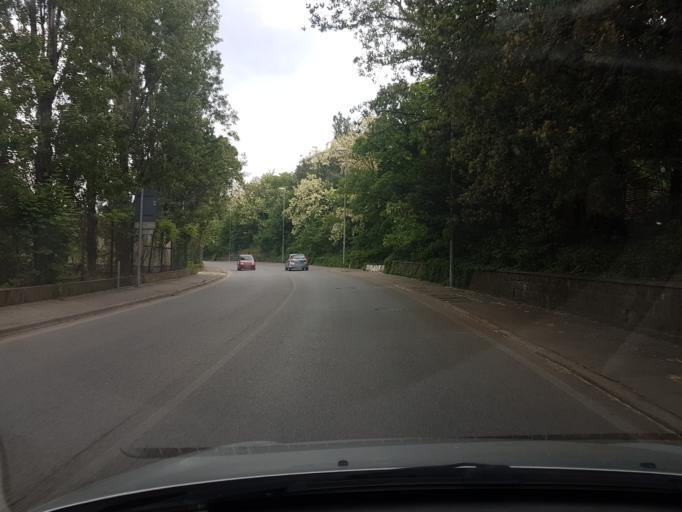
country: IT
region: Friuli Venezia Giulia
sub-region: Provincia di Trieste
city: Muggia
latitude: 45.5997
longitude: 13.7781
